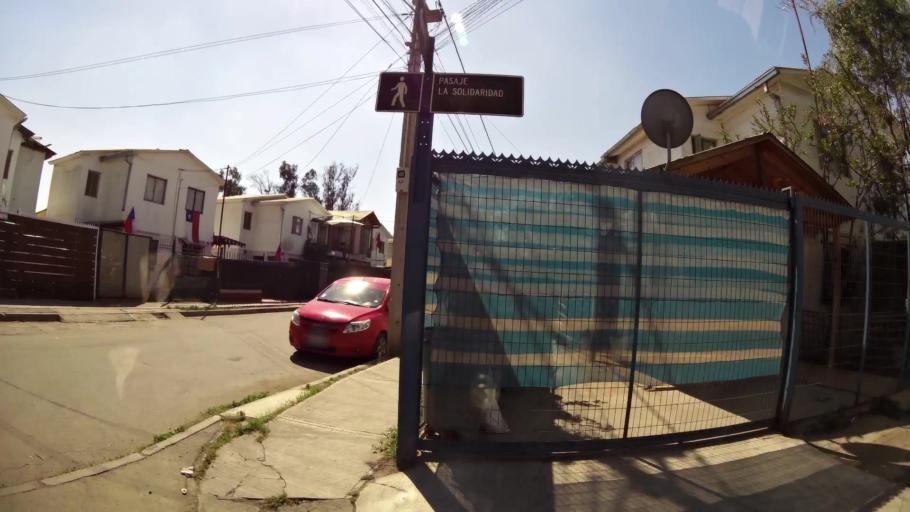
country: CL
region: Santiago Metropolitan
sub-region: Provincia de Cordillera
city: Puente Alto
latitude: -33.6286
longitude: -70.6094
